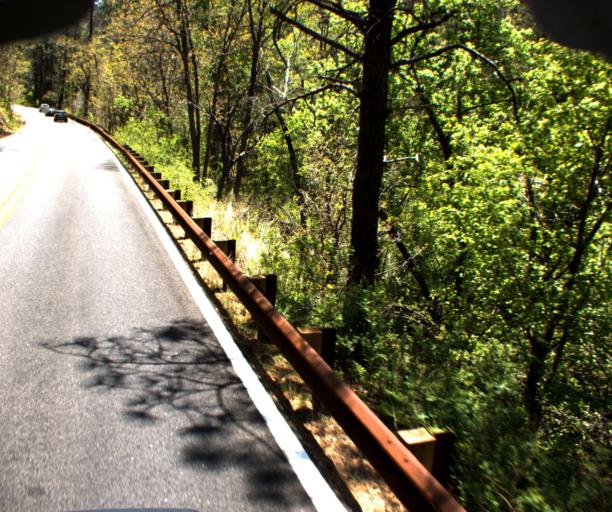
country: US
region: Arizona
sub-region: Coconino County
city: Kachina Village
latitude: 35.0199
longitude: -111.7368
